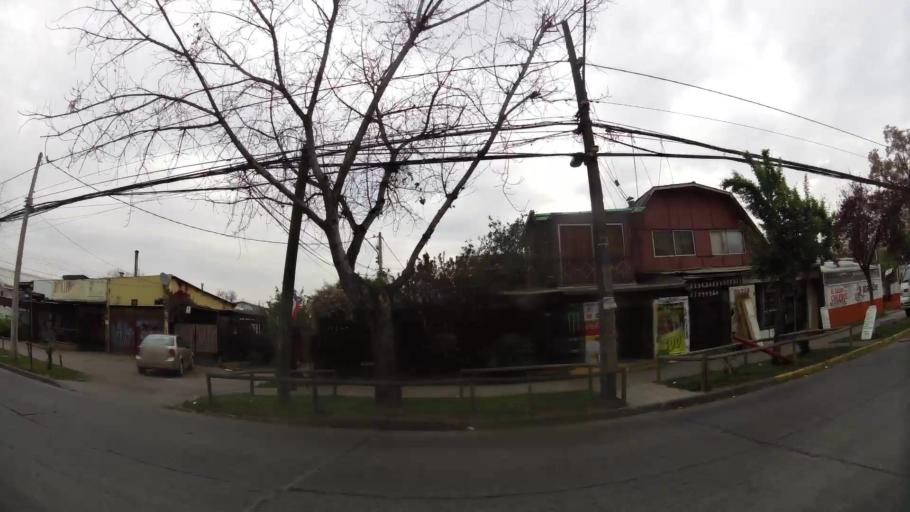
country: CL
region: Santiago Metropolitan
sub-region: Provincia de Santiago
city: Villa Presidente Frei, Nunoa, Santiago, Chile
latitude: -33.4683
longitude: -70.5819
